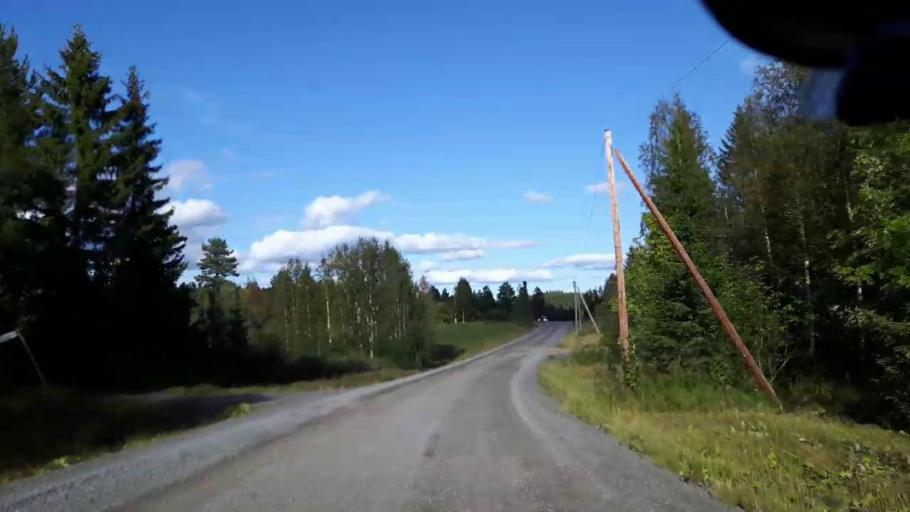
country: SE
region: Jaemtland
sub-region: Ragunda Kommun
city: Hammarstrand
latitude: 63.4330
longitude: 16.1816
